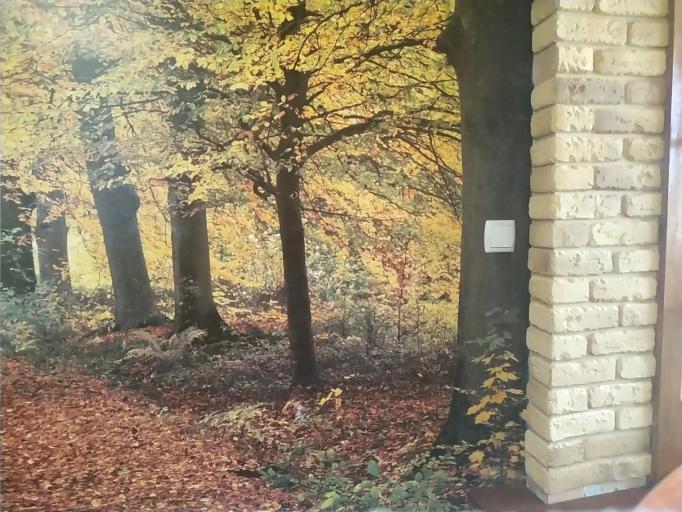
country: RU
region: Tverskaya
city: Vyshniy Volochek
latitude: 57.6868
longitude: 34.5108
